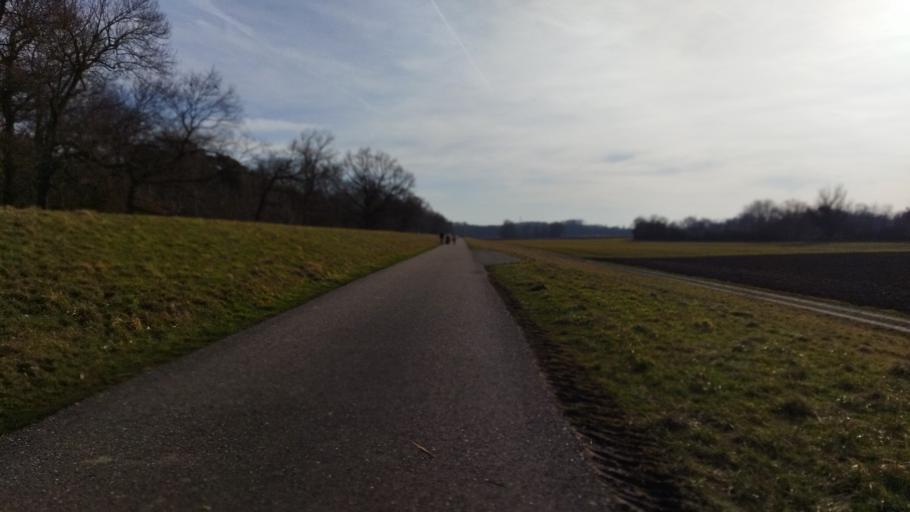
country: DE
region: Rheinland-Pfalz
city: Leimersheim
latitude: 49.1174
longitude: 8.3531
